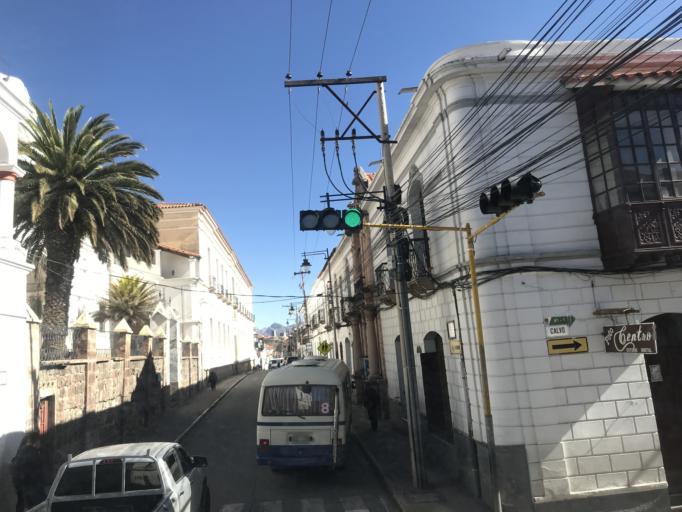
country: BO
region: Chuquisaca
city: Sucre
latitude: -19.0486
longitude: -65.2578
